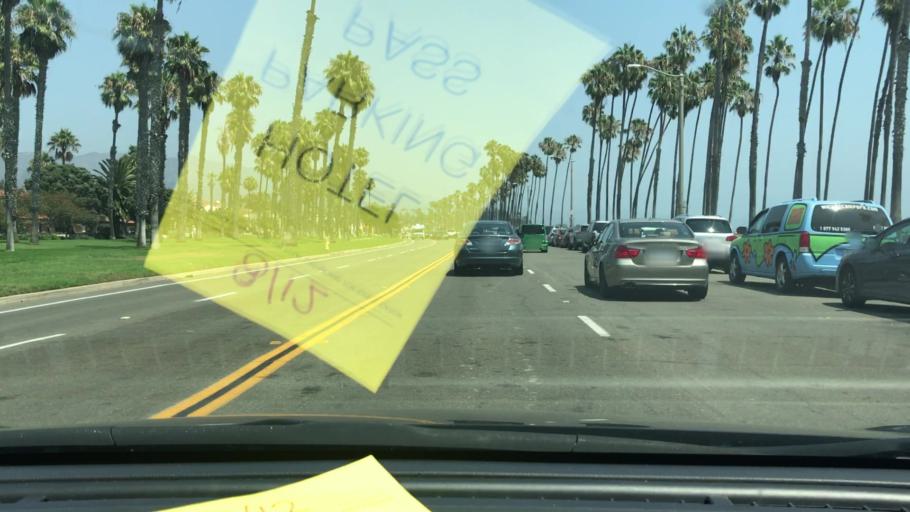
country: US
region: California
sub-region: Santa Barbara County
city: Santa Barbara
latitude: 34.4155
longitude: -119.6791
